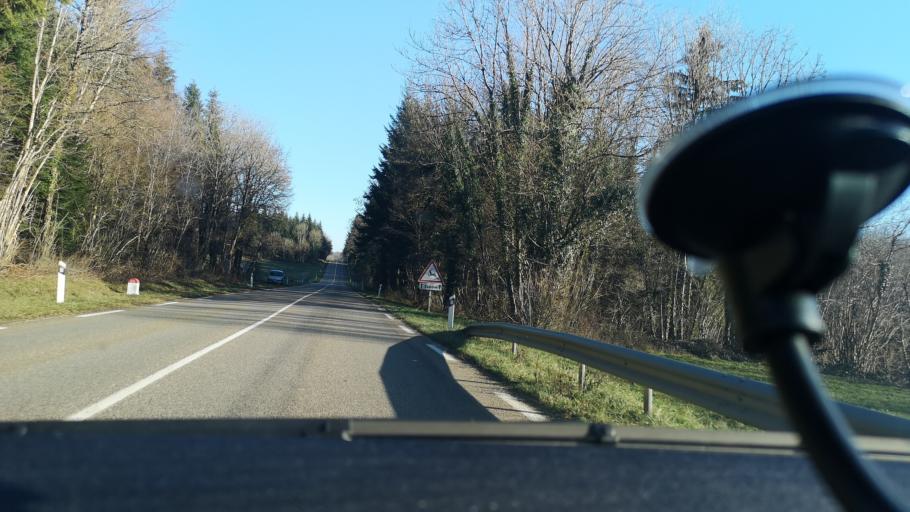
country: FR
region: Franche-Comte
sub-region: Departement du Jura
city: Poligny
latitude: 46.8173
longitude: 5.7420
